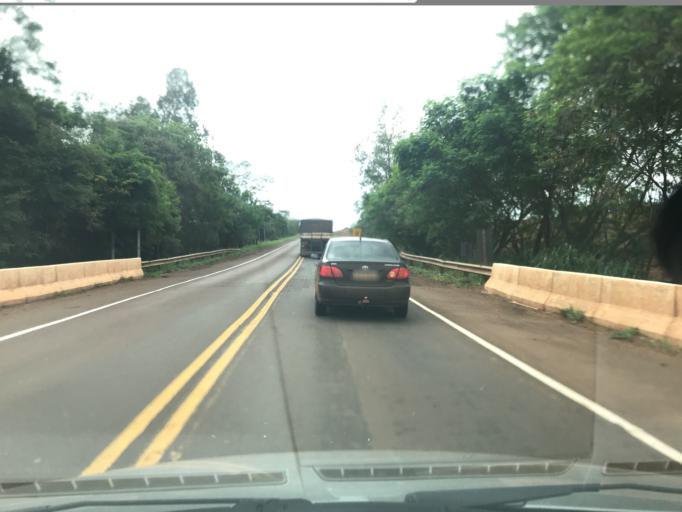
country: BR
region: Parana
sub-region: Terra Boa
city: Terra Boa
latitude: -23.6151
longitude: -52.4301
